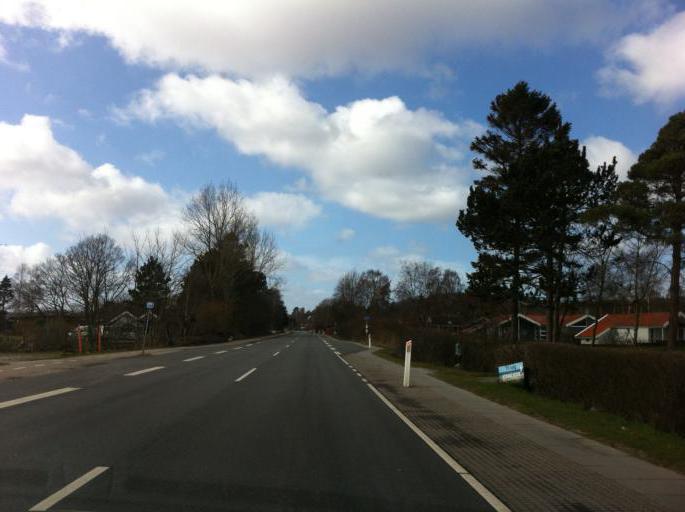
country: DK
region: Central Jutland
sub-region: Syddjurs Kommune
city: Ebeltoft
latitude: 56.2280
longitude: 10.6259
